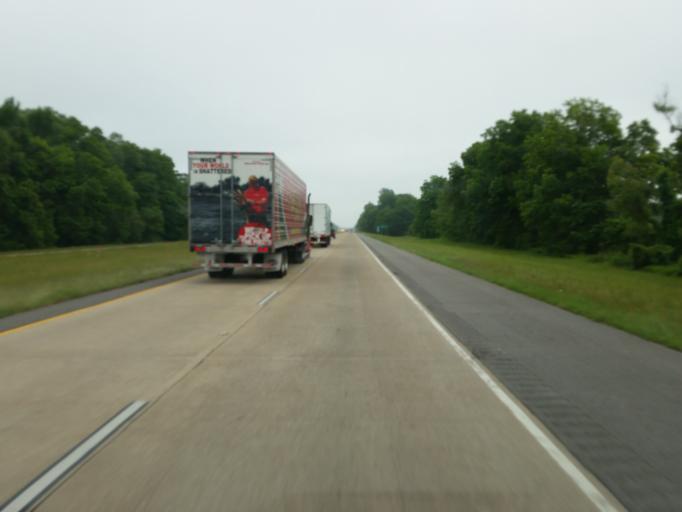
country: US
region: Louisiana
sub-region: Madison Parish
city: Tallulah
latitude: 32.3760
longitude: -91.1584
